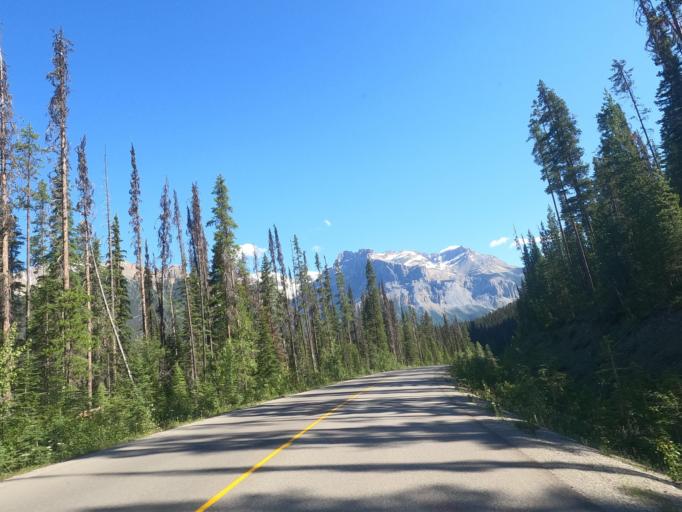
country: CA
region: Alberta
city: Lake Louise
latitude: 51.4191
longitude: -116.5339
